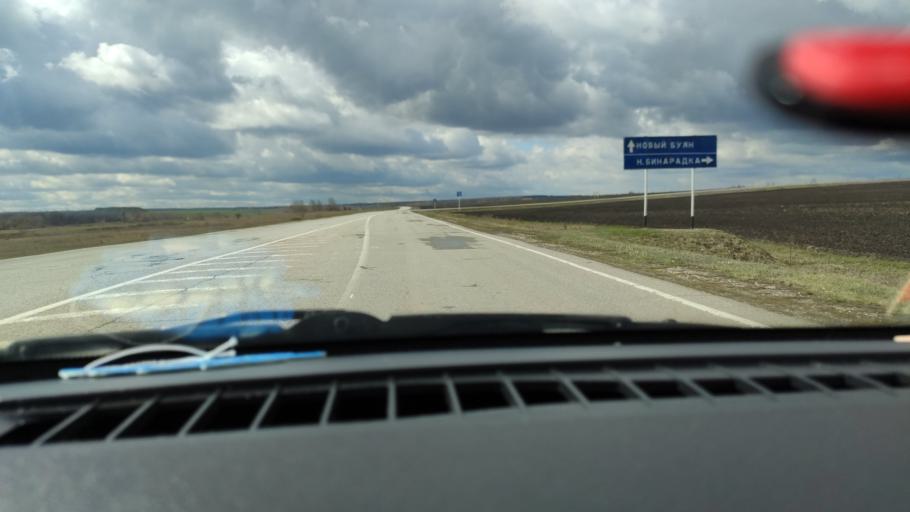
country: RU
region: Samara
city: Novyy Buyan
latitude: 53.7728
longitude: 50.0241
